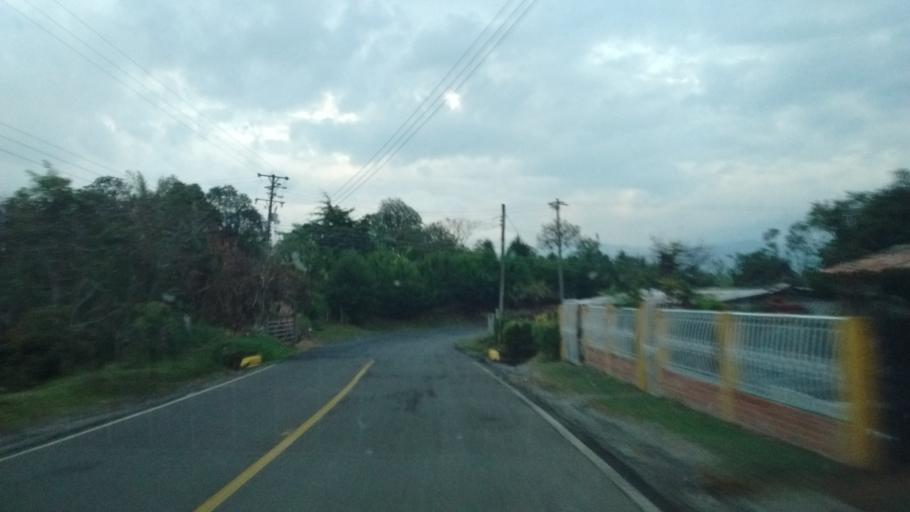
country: CO
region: Cauca
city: Popayan
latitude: 2.3778
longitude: -76.7015
